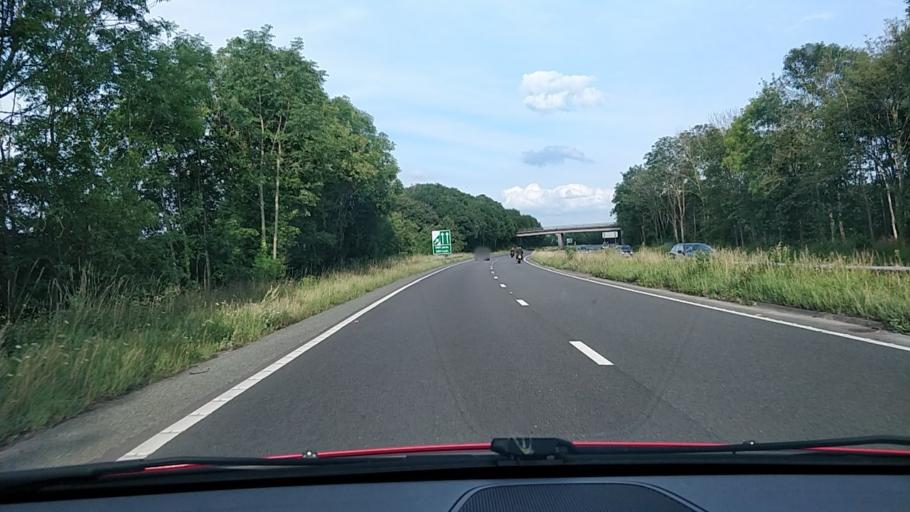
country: GB
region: Wales
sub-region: County of Flintshire
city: Hawarden
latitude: 53.1634
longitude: -2.9736
